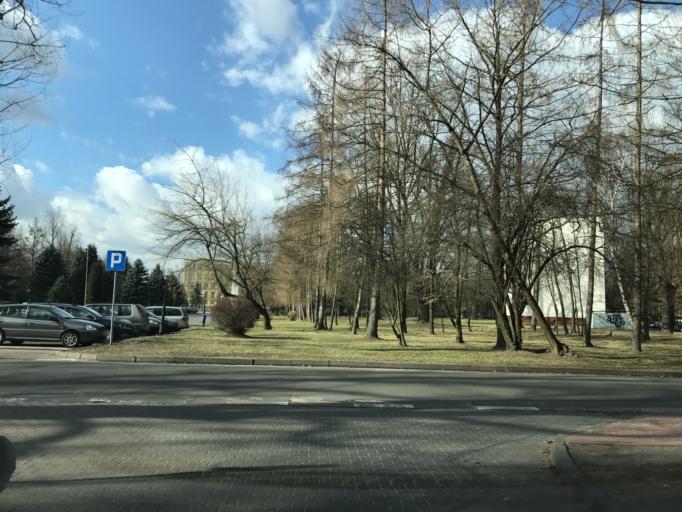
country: PL
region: Masovian Voivodeship
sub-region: Warszawa
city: Rembertow
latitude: 52.2659
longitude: 21.1779
